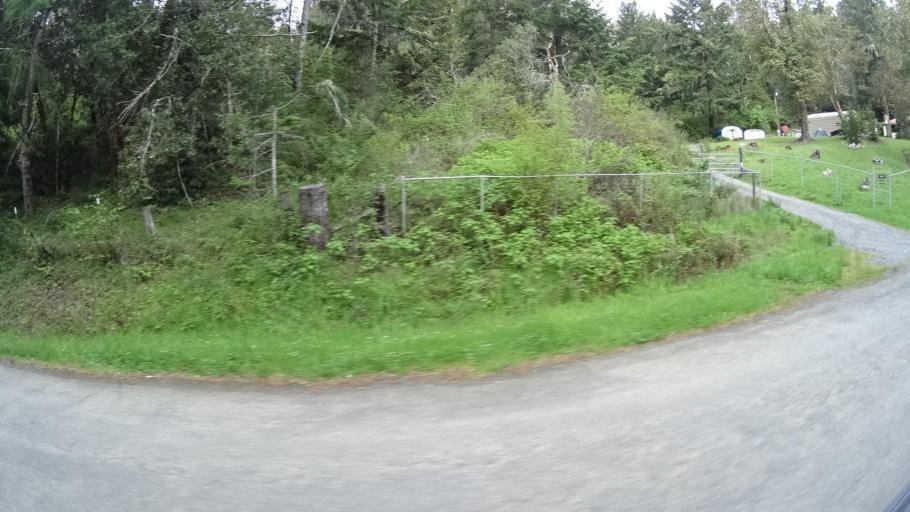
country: US
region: California
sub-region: Humboldt County
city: Redway
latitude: 40.3005
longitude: -123.8219
